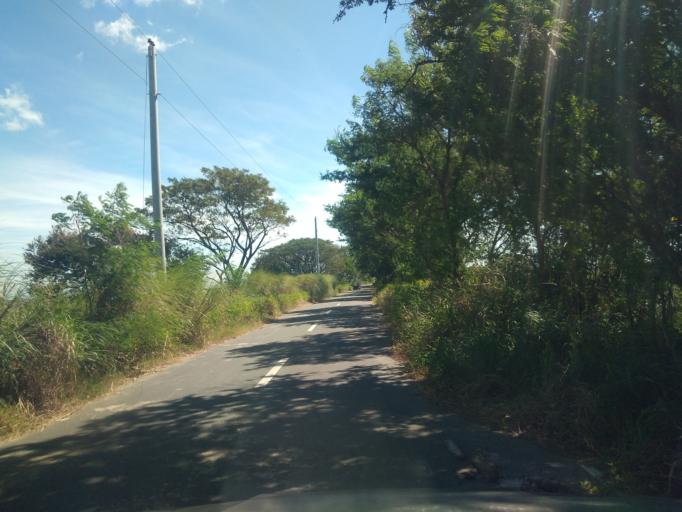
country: PH
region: Central Luzon
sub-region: Province of Pampanga
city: Balas
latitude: 15.0496
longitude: 120.5875
